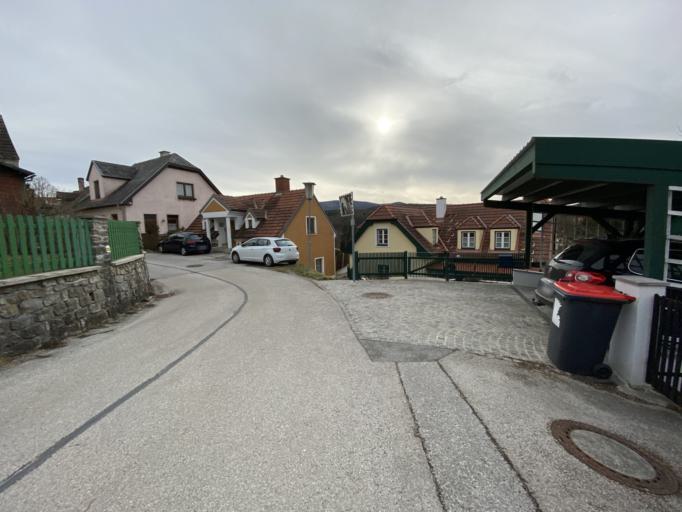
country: AT
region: Lower Austria
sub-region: Politischer Bezirk Modling
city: Gaaden
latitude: 48.0367
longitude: 16.1761
